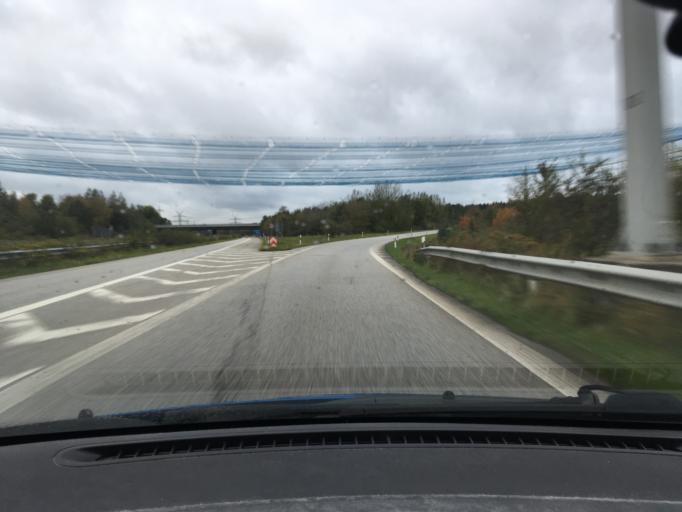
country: DE
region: Schleswig-Holstein
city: Schulldorf
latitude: 54.3069
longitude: 9.7595
